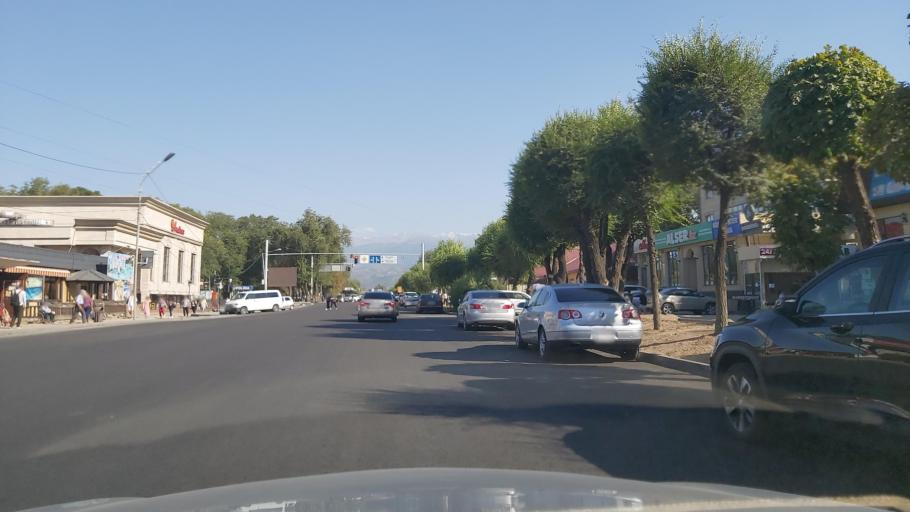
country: KZ
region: Almaty Oblysy
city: Pervomayskiy
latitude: 43.3218
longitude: 76.9138
